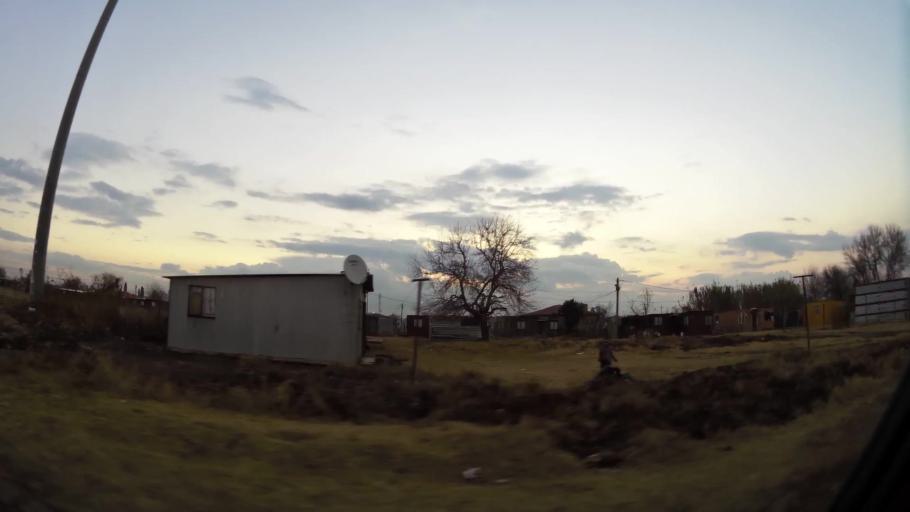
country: ZA
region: Gauteng
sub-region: City of Johannesburg Metropolitan Municipality
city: Orange Farm
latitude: -26.5536
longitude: 27.8482
